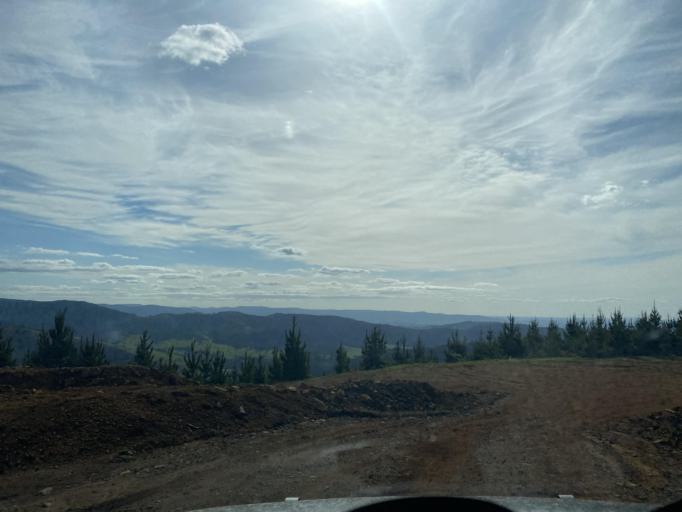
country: AU
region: Victoria
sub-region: Mansfield
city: Mansfield
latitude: -36.8332
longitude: 146.1785
